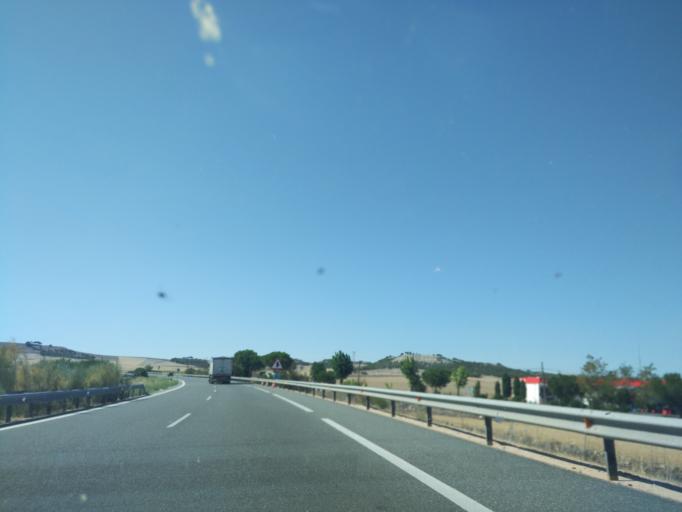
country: ES
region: Castille and Leon
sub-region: Provincia de Valladolid
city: Vega de Valdetronco
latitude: 41.5966
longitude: -5.1222
